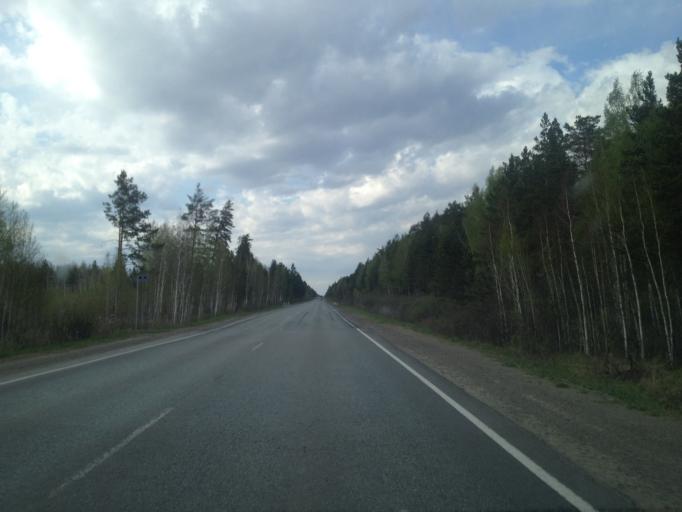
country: RU
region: Kurgan
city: Krasnyy Oktyabr'
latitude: 55.7317
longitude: 64.9040
